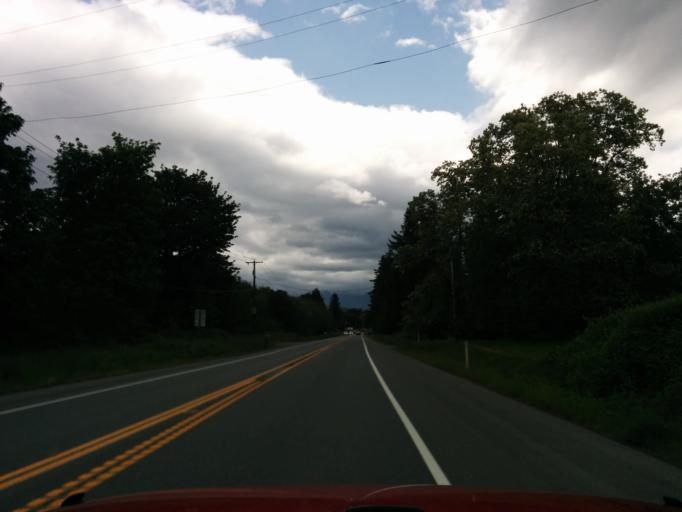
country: US
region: Washington
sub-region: King County
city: Fall City
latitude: 47.5722
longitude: -121.9033
